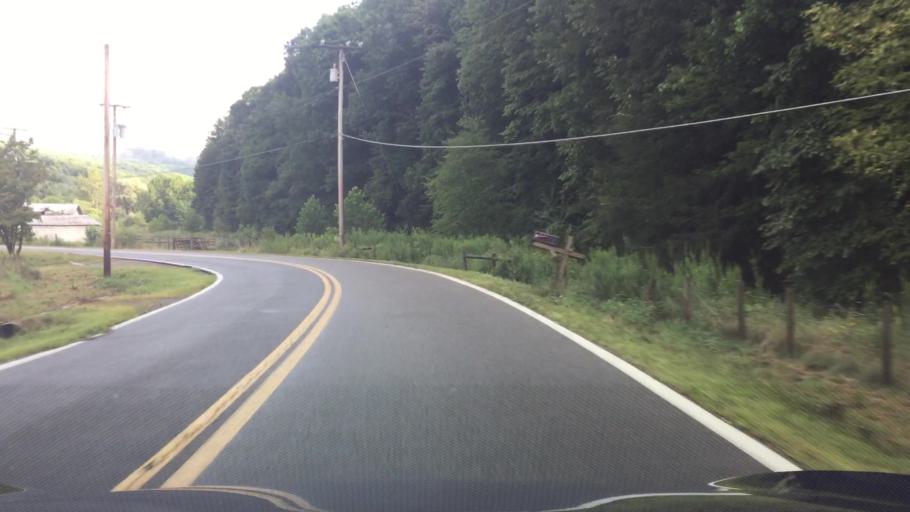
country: US
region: Virginia
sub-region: Smyth County
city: Atkins
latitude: 36.8558
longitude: -81.4299
